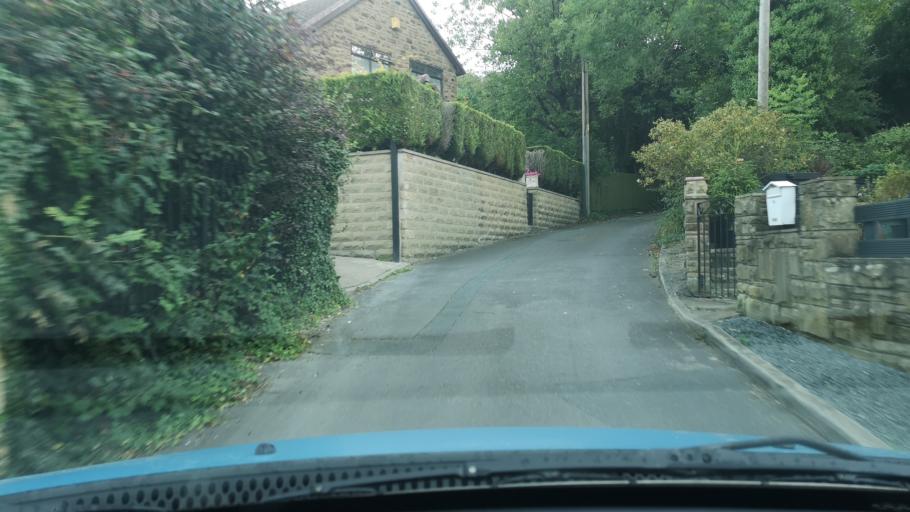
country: GB
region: England
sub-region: City and Borough of Wakefield
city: Fitzwilliam
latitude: 53.6440
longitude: -1.3571
